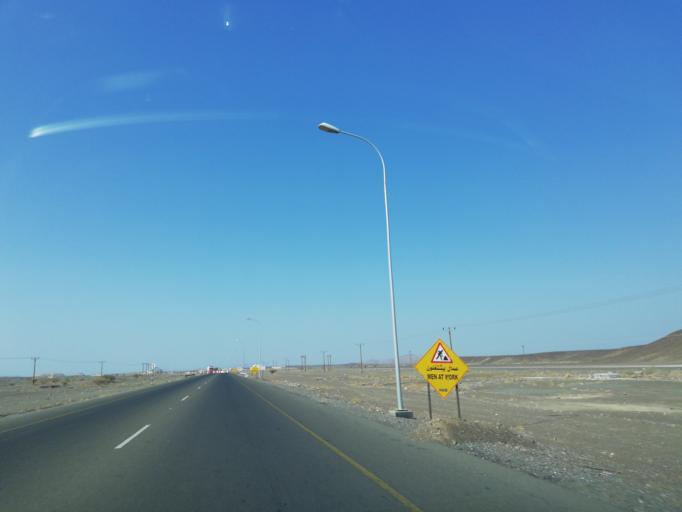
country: OM
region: Ash Sharqiyah
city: Ibra'
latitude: 22.7135
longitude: 58.1453
